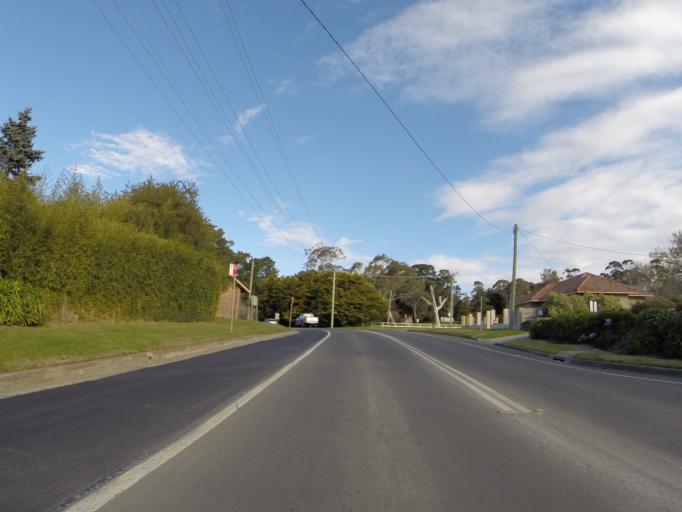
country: AU
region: New South Wales
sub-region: Wingecarribee
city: Moss Vale
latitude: -34.5471
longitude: 150.3802
